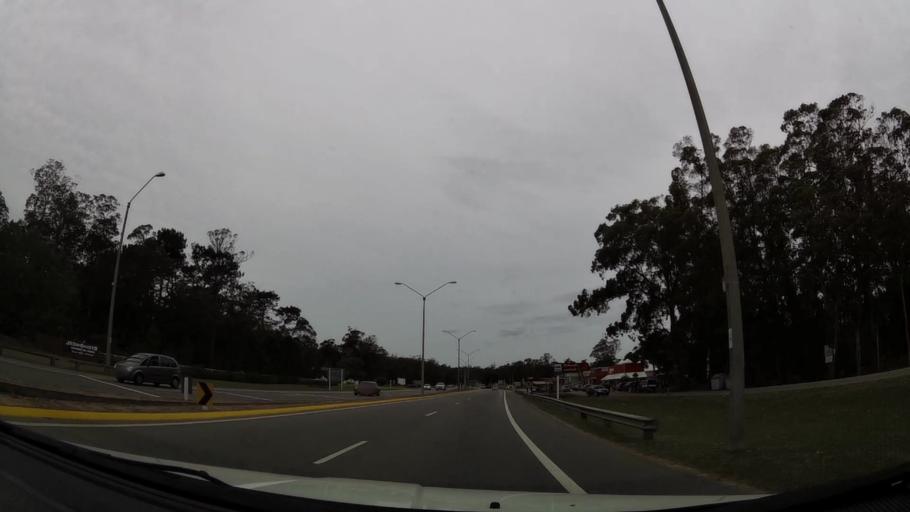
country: UY
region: Maldonado
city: Maldonado
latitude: -34.8804
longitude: -55.0499
